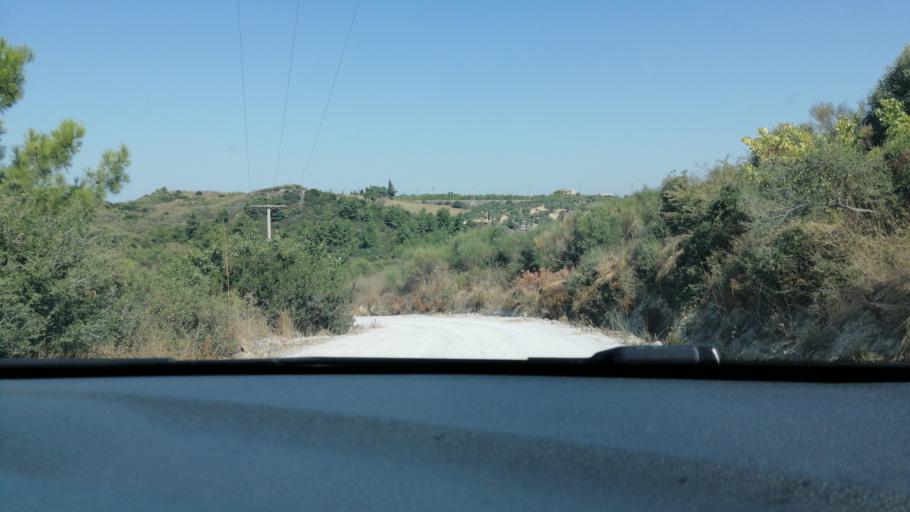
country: TR
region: Aydin
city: Davutlar
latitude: 37.7804
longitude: 27.3136
